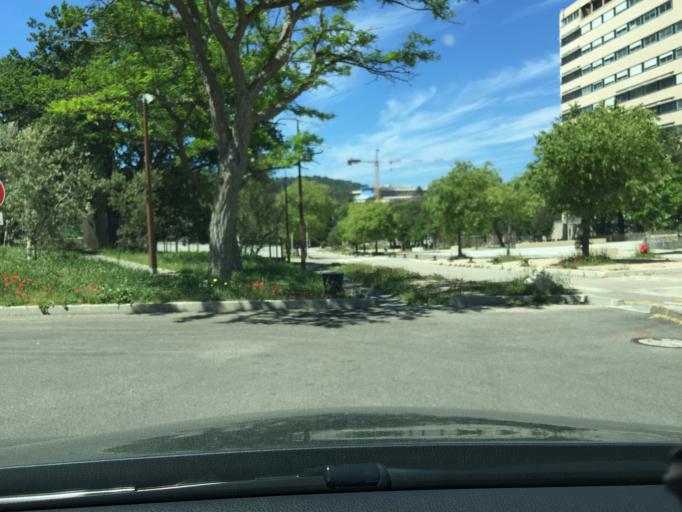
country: FR
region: Provence-Alpes-Cote d'Azur
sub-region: Departement des Bouches-du-Rhone
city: Marseille 09
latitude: 43.2312
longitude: 5.4405
